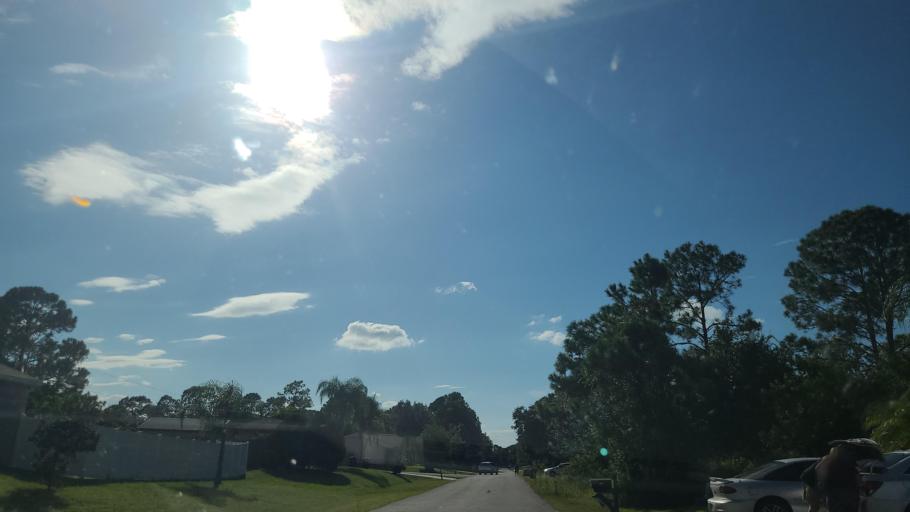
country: US
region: Florida
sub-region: Brevard County
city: West Melbourne
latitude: 27.9804
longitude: -80.6662
